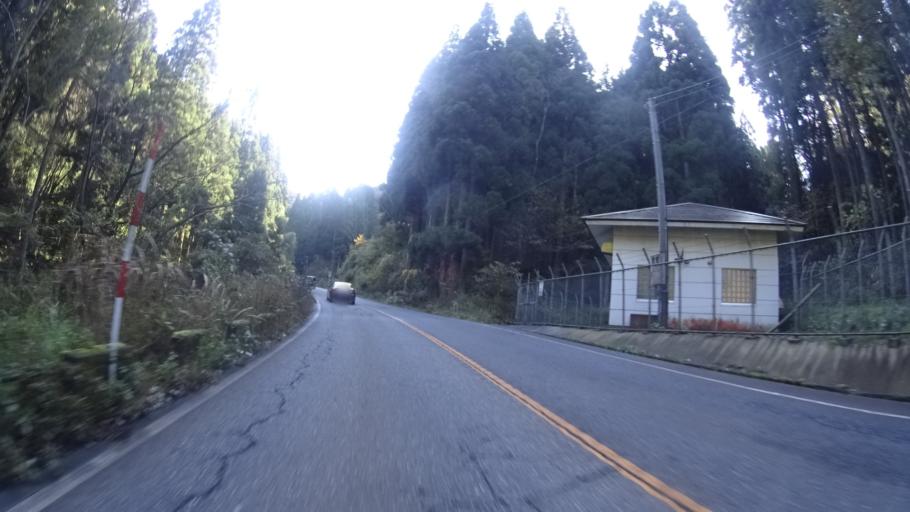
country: JP
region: Ishikawa
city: Tsurugi-asahimachi
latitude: 36.3722
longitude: 136.5775
